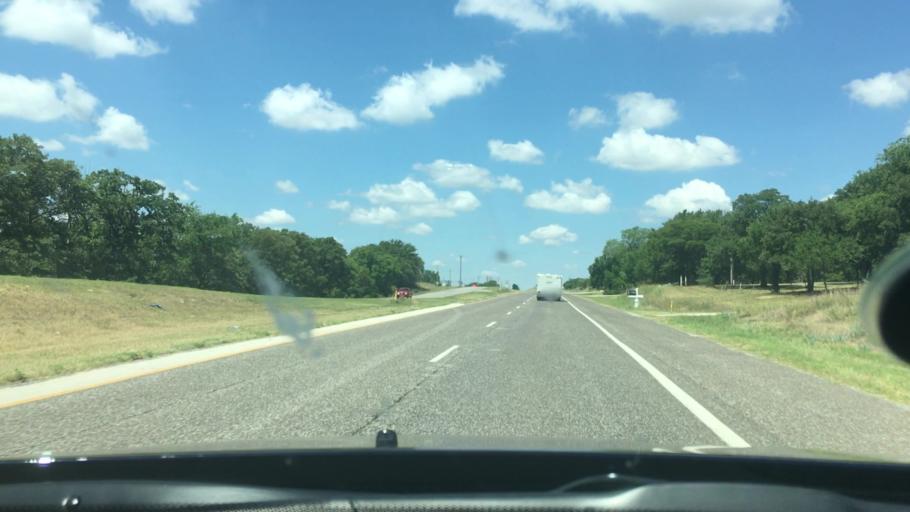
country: US
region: Oklahoma
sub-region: Carter County
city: Lone Grove
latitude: 34.1730
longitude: -97.3235
